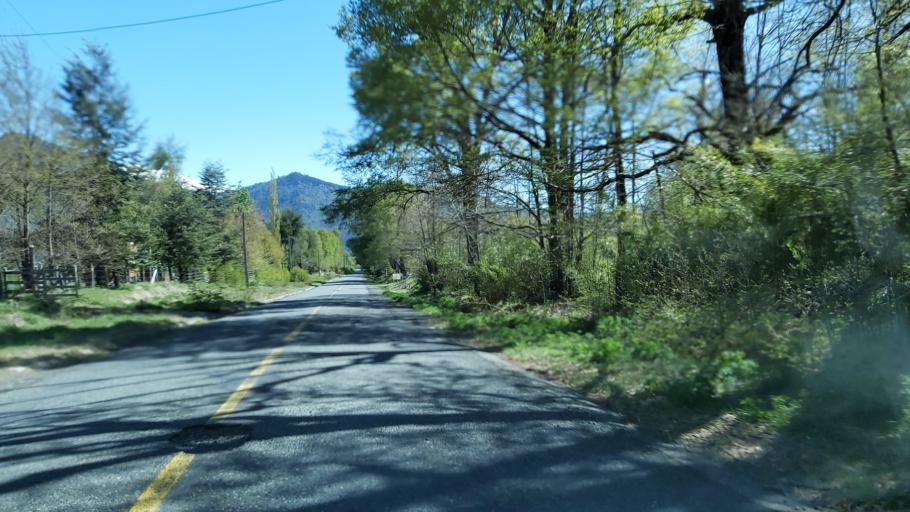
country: CL
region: Araucania
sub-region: Provincia de Cautin
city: Vilcun
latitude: -38.4677
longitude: -71.5212
